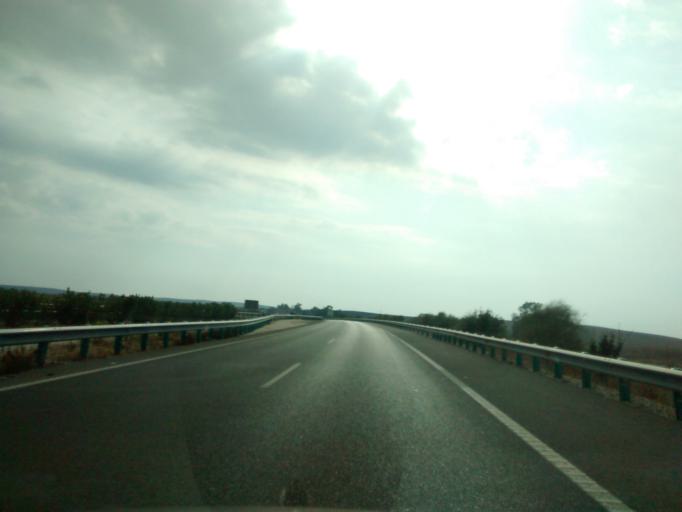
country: ES
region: Andalusia
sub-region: Provincia de Cadiz
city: Arcos de la Frontera
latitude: 36.7398
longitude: -5.8841
